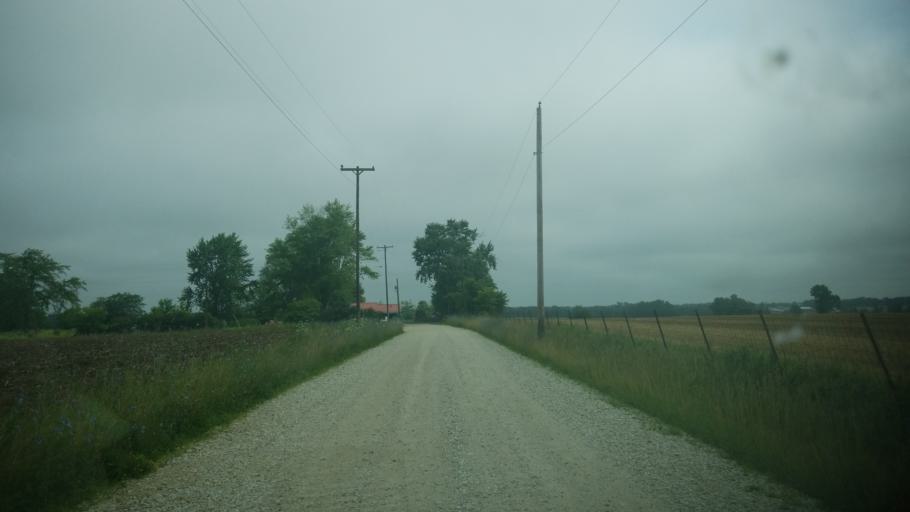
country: US
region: Missouri
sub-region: Pike County
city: Bowling Green
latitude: 39.3486
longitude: -91.2559
